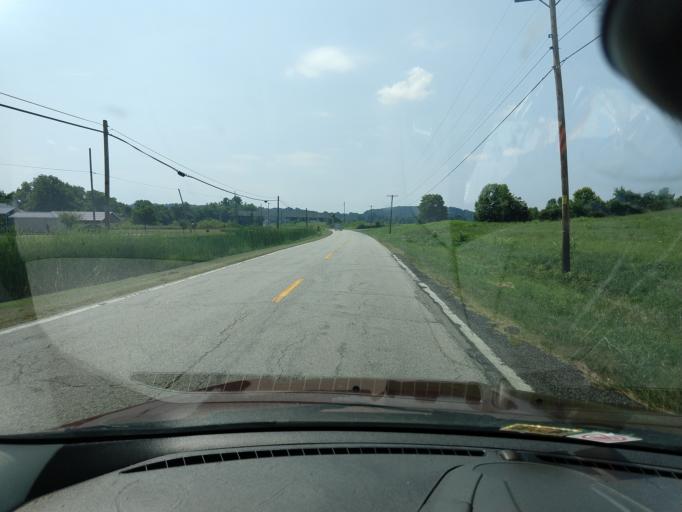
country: US
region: West Virginia
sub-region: Mason County
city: New Haven
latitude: 38.8915
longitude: -81.9328
